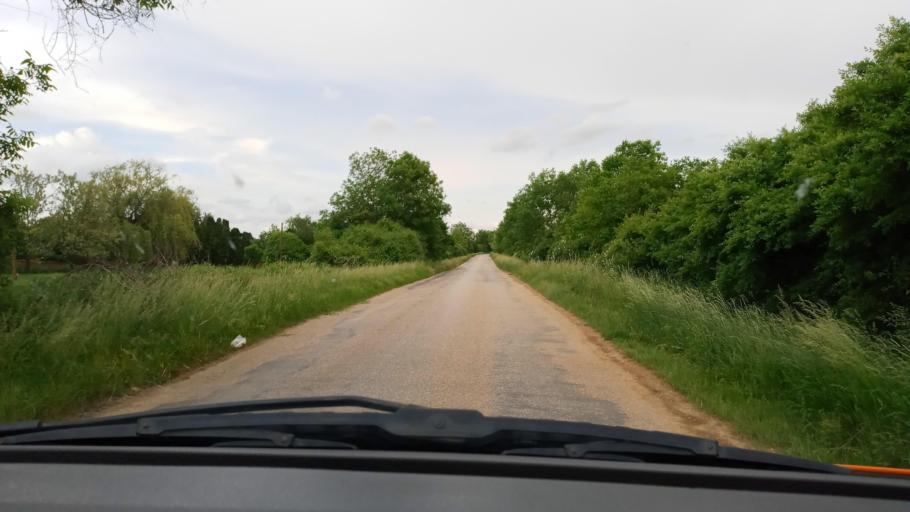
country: HU
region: Baranya
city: Harkany
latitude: 45.9169
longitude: 18.1548
